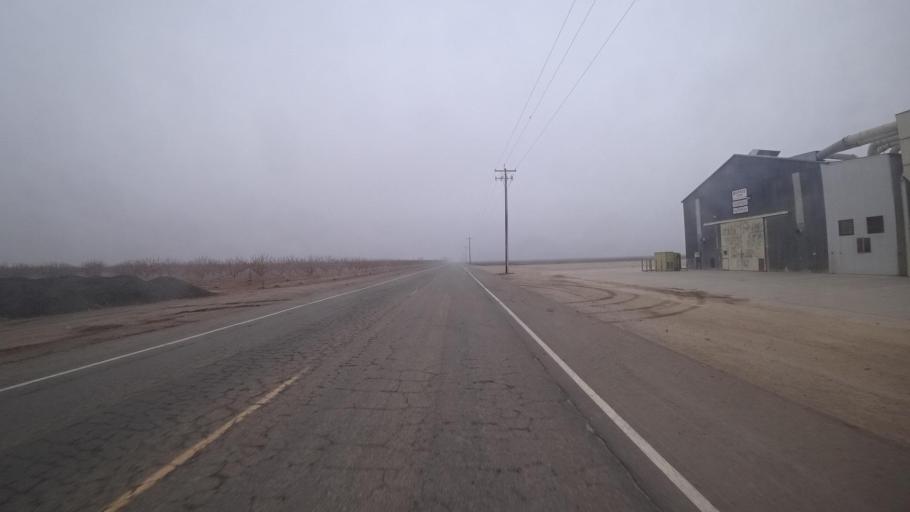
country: US
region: California
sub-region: Kern County
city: Buttonwillow
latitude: 35.4280
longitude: -119.5183
